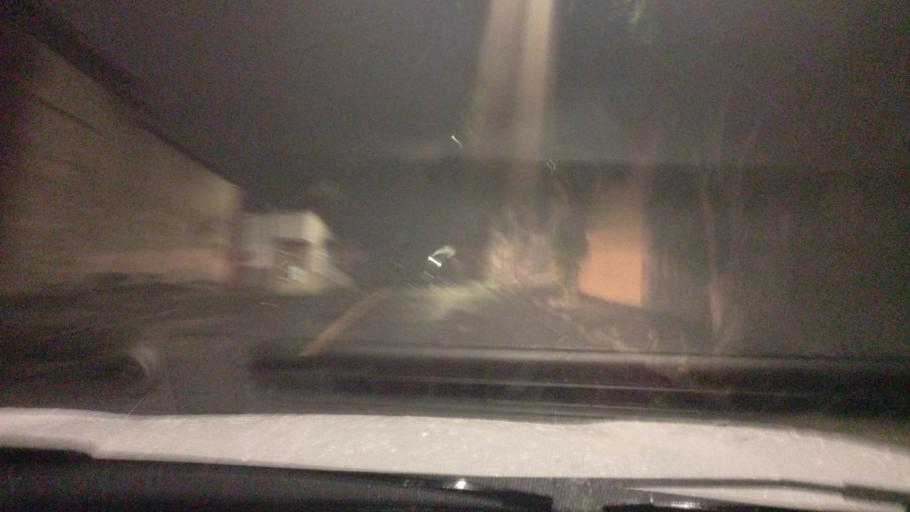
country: BR
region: Minas Gerais
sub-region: Belo Horizonte
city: Belo Horizonte
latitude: -19.9014
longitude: -43.9190
